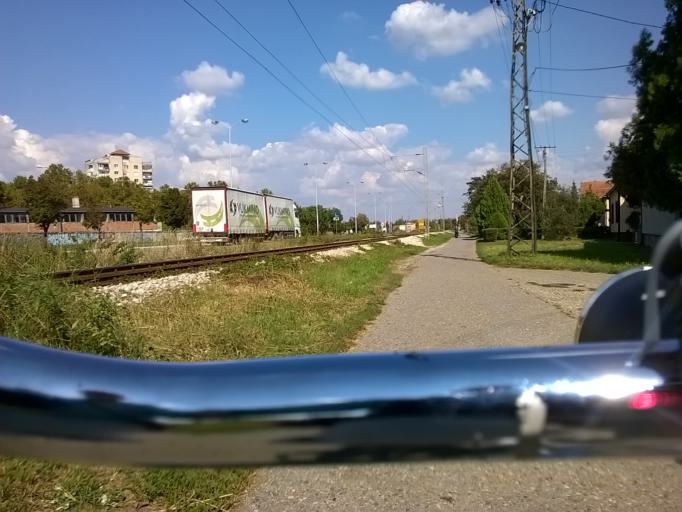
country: RS
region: Autonomna Pokrajina Vojvodina
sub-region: Juznobanatski Okrug
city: Pancevo
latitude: 44.8685
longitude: 20.6644
